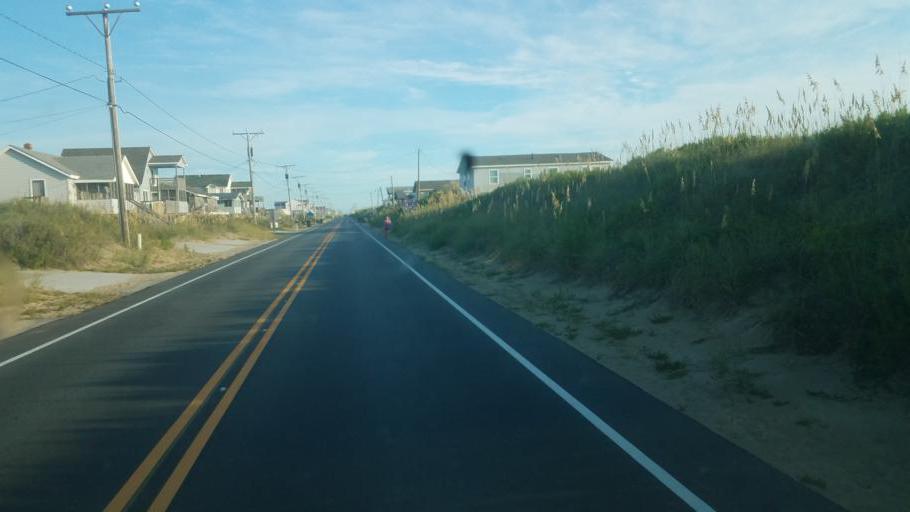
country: US
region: North Carolina
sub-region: Dare County
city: Kill Devil Hills
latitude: 36.0541
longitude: -75.6818
